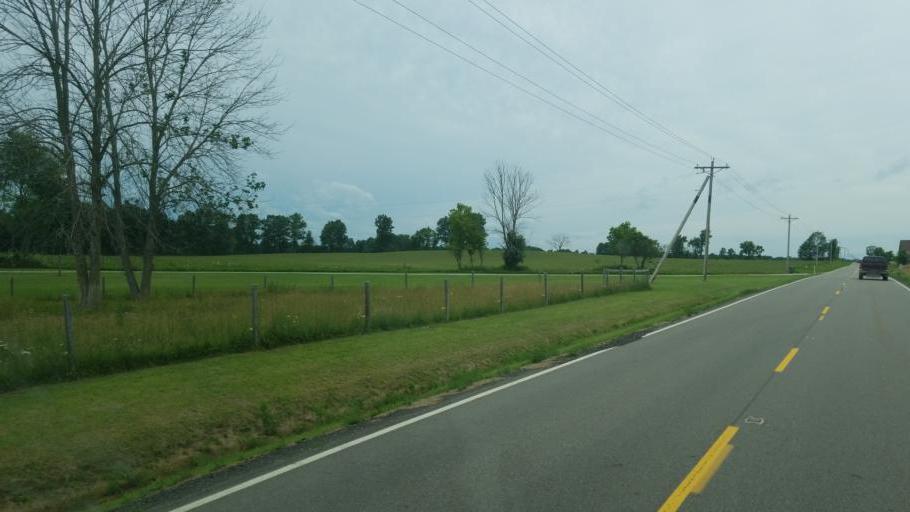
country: US
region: Ohio
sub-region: Licking County
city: Utica
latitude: 40.2330
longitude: -82.5676
